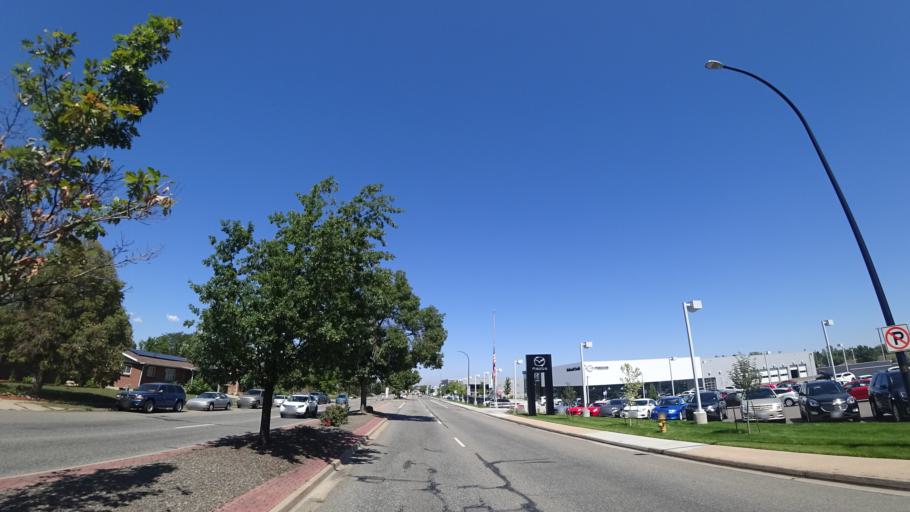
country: US
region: Colorado
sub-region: Arapahoe County
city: Littleton
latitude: 39.6049
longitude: -104.9881
